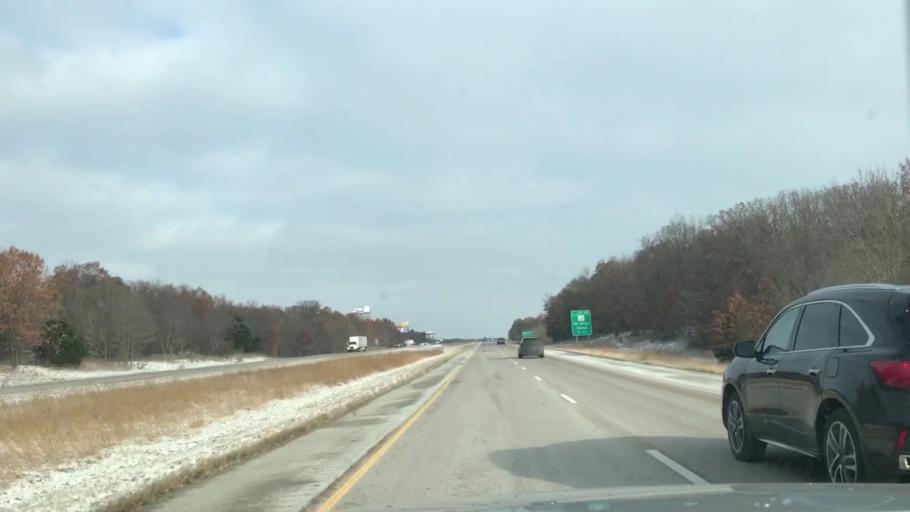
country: US
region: Illinois
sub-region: Macoupin County
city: Mount Olive
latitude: 39.0597
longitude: -89.7556
